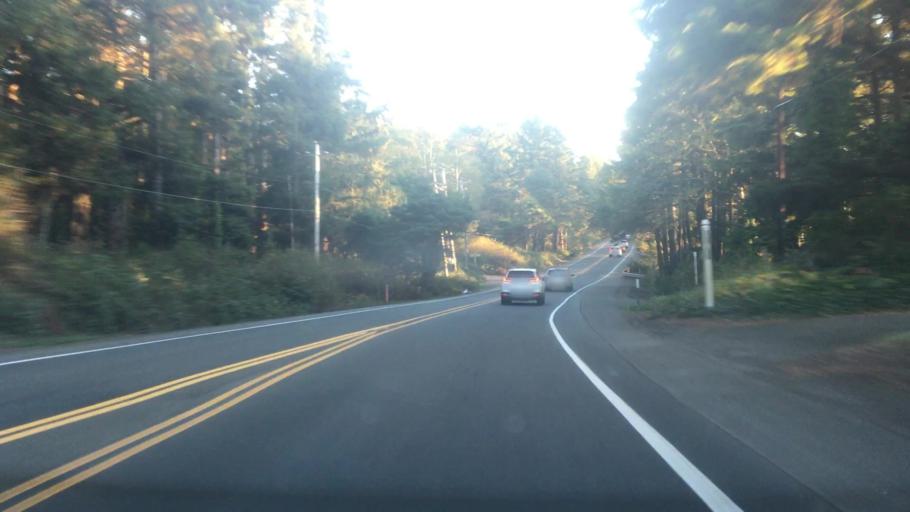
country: US
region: Oregon
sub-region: Clatsop County
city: Cannon Beach
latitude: 45.8458
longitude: -123.9596
